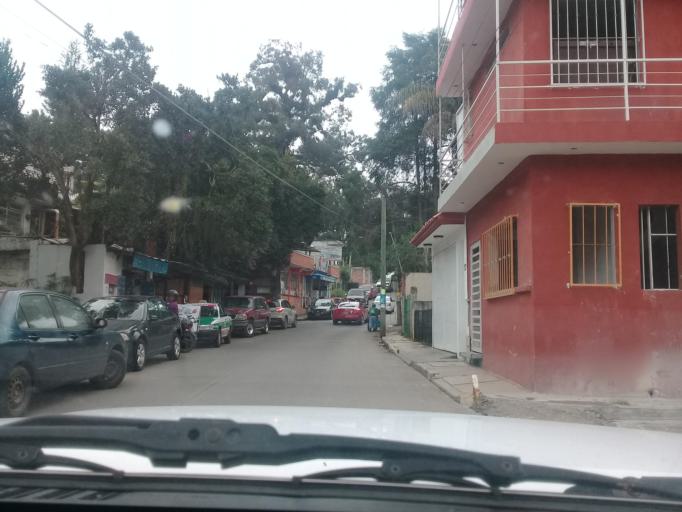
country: MX
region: Veracruz
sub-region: Xalapa
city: Xalapa de Enriquez
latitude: 19.5128
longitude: -96.9114
